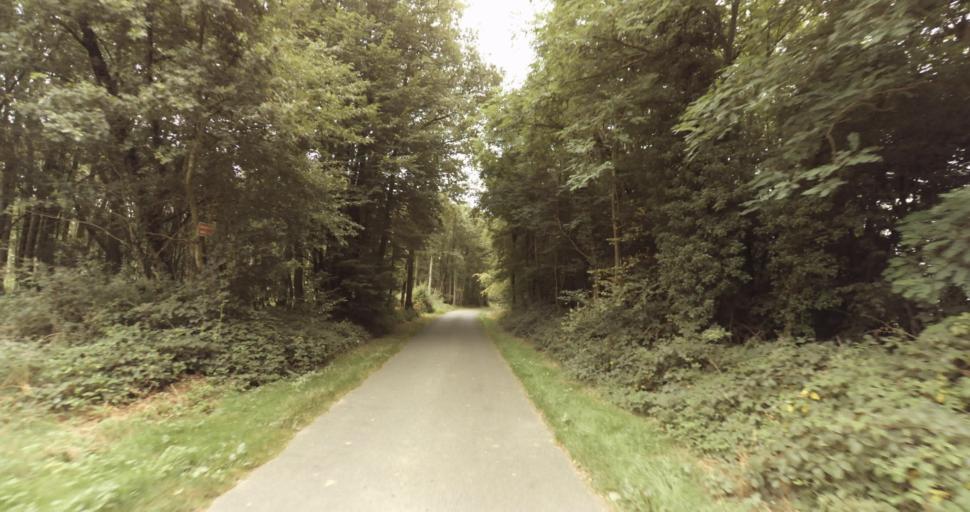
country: FR
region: Centre
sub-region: Departement d'Eure-et-Loir
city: Vert-en-Drouais
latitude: 48.7994
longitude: 1.2878
